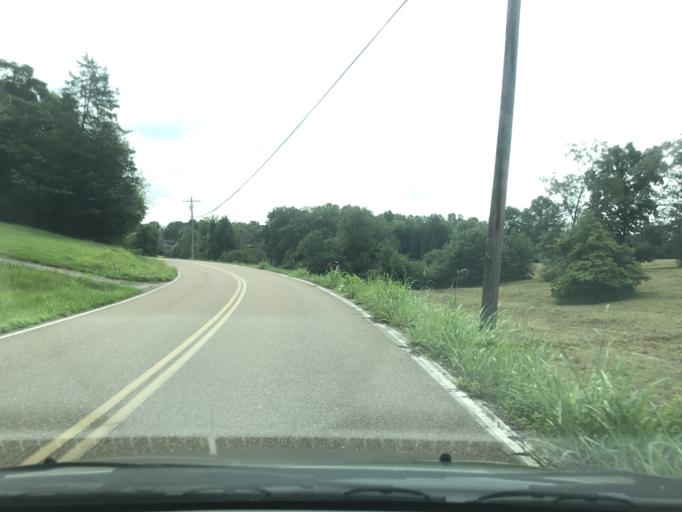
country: US
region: Tennessee
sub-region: Hamilton County
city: Lakesite
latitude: 35.2056
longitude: -85.0768
